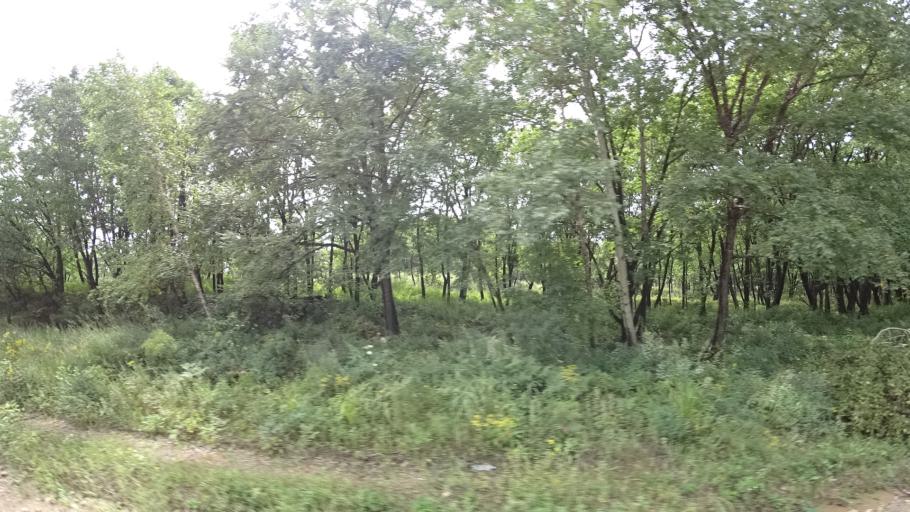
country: RU
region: Primorskiy
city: Lyalichi
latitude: 44.0930
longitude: 132.4328
